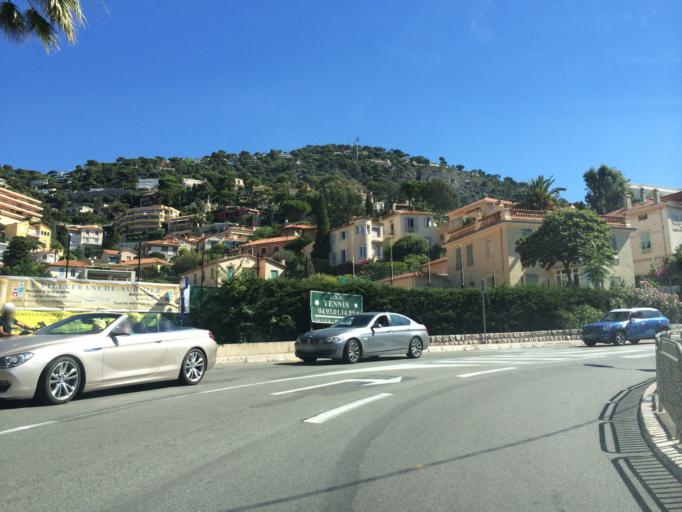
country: FR
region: Provence-Alpes-Cote d'Azur
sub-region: Departement des Alpes-Maritimes
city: Villefranche-sur-Mer
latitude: 43.7058
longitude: 7.3097
